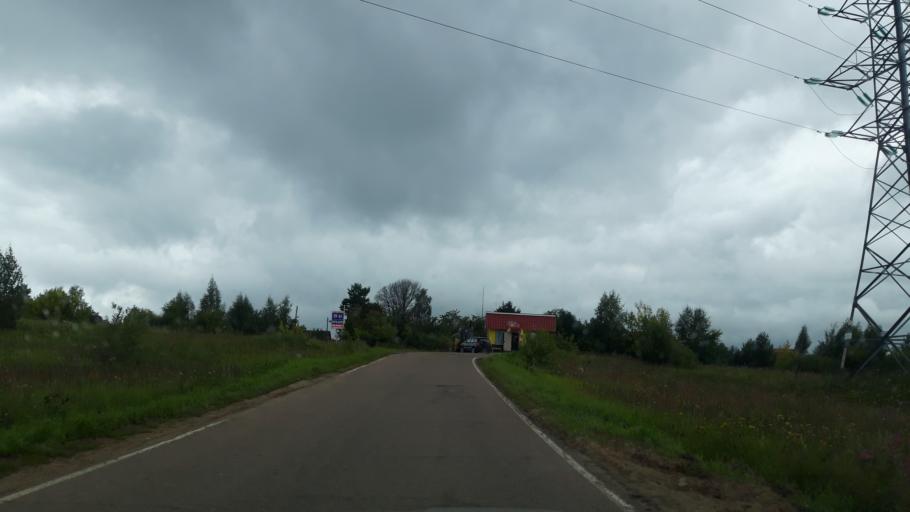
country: RU
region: Moskovskaya
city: Lozhki
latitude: 56.0916
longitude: 37.0746
